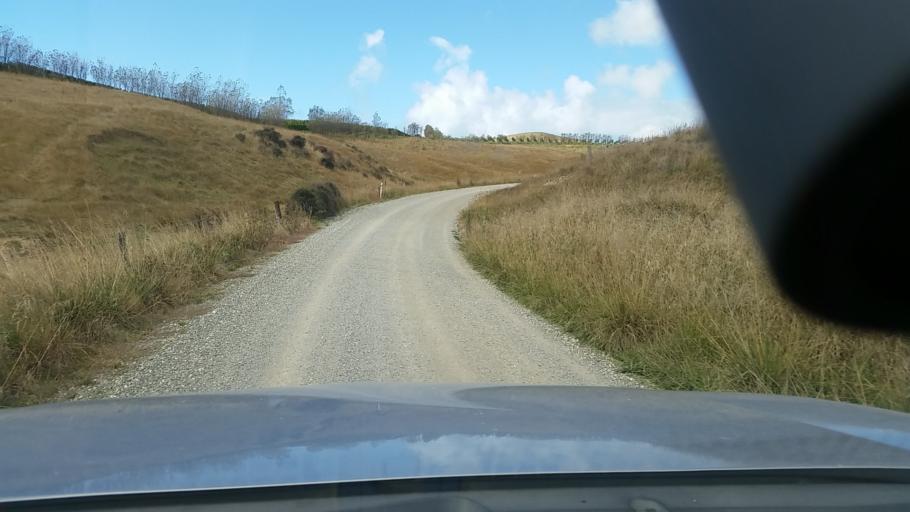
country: NZ
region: Marlborough
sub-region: Marlborough District
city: Blenheim
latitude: -41.6887
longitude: 174.1391
